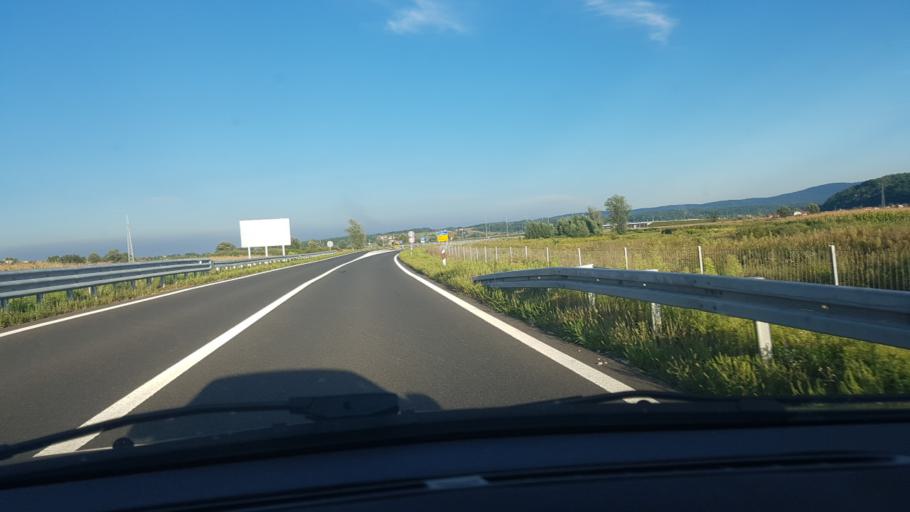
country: HR
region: Krapinsko-Zagorska
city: Selnica
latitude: 46.0410
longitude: 16.0642
